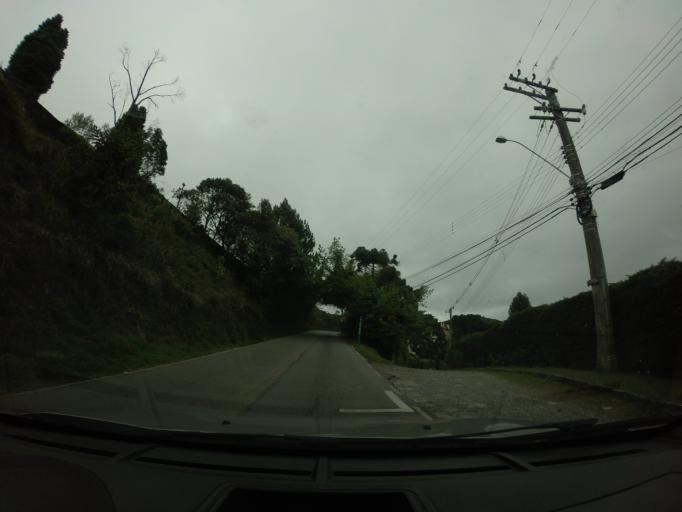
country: BR
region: Sao Paulo
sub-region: Campos Do Jordao
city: Campos do Jordao
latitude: -22.7149
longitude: -45.5827
